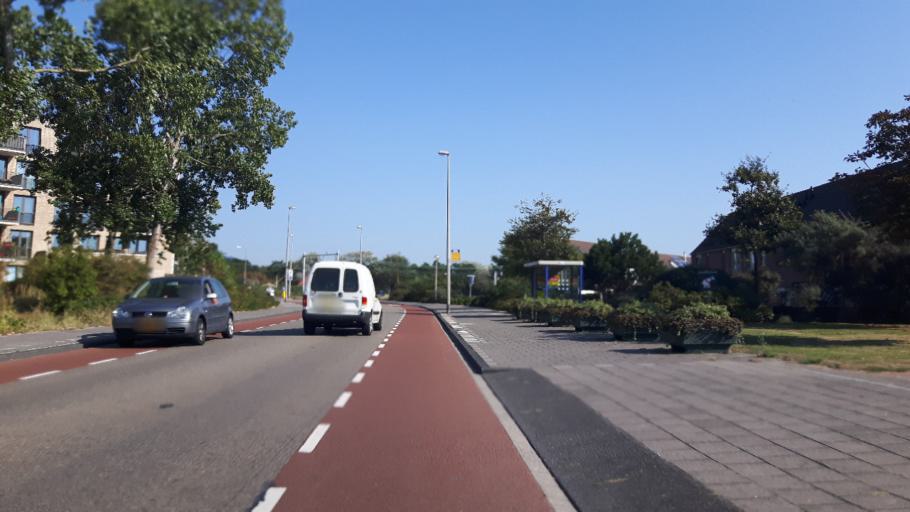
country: NL
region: North Holland
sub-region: Gemeente Zandvoort
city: Zandvoort
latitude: 52.3735
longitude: 4.5403
